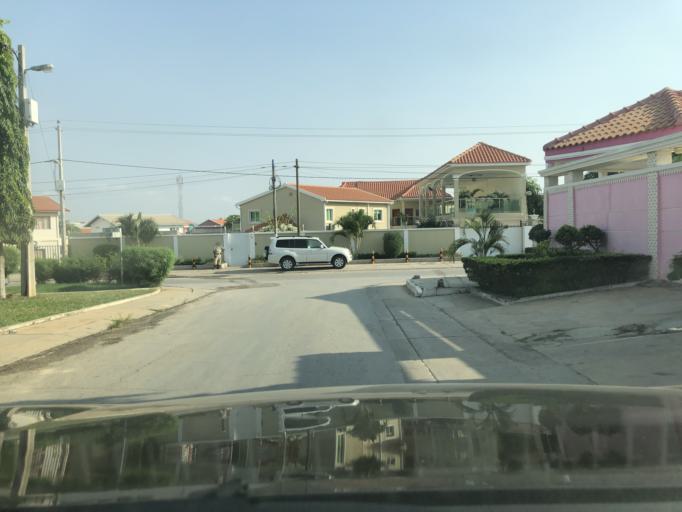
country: AO
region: Luanda
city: Luanda
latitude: -8.9087
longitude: 13.2269
